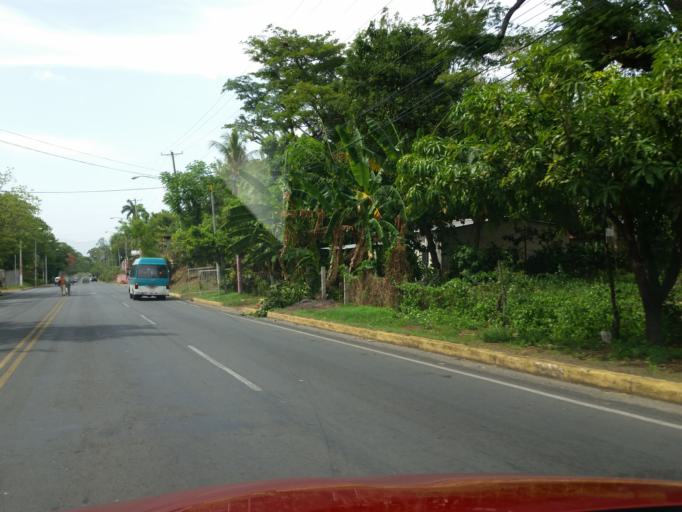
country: NI
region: Managua
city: Ciudad Sandino
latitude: 12.0788
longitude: -86.3239
